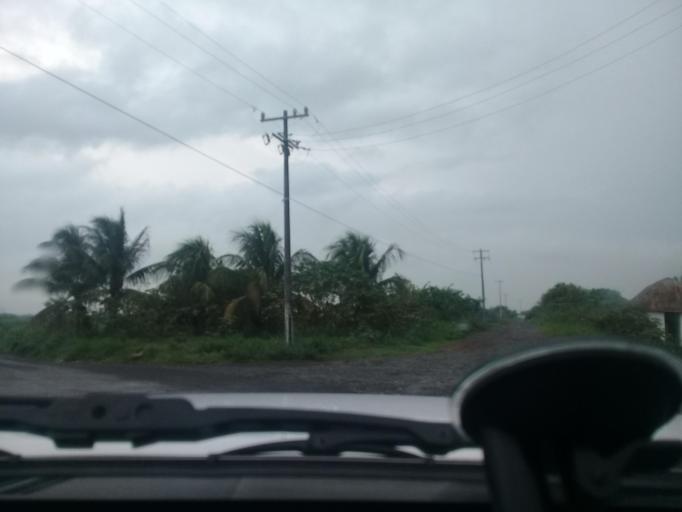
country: MX
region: Veracruz
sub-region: La Antigua
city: Nicolas Blanco (San Pancho)
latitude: 19.3518
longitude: -96.3439
